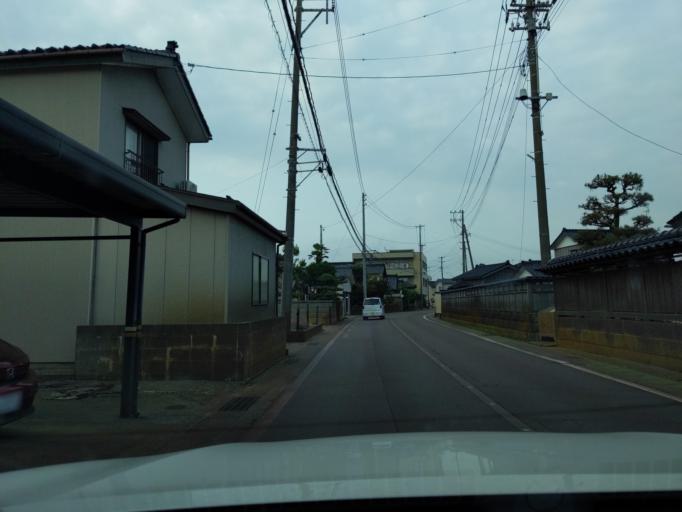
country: JP
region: Niigata
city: Kashiwazaki
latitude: 37.3848
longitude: 138.5766
